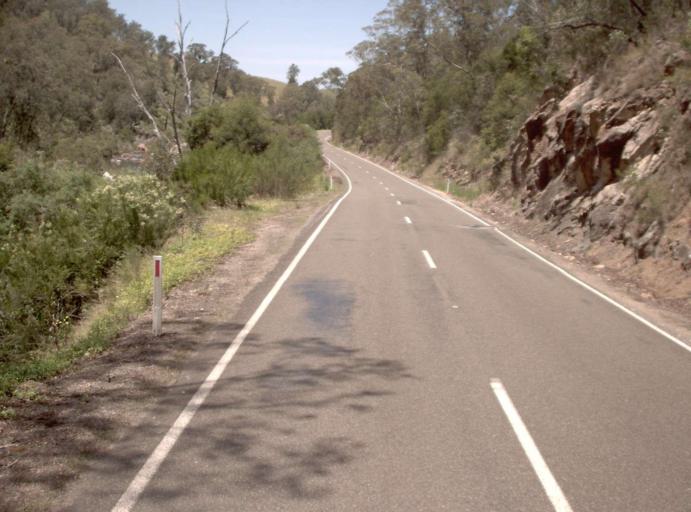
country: AU
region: Victoria
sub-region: East Gippsland
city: Bairnsdale
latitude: -37.4881
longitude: 147.8330
